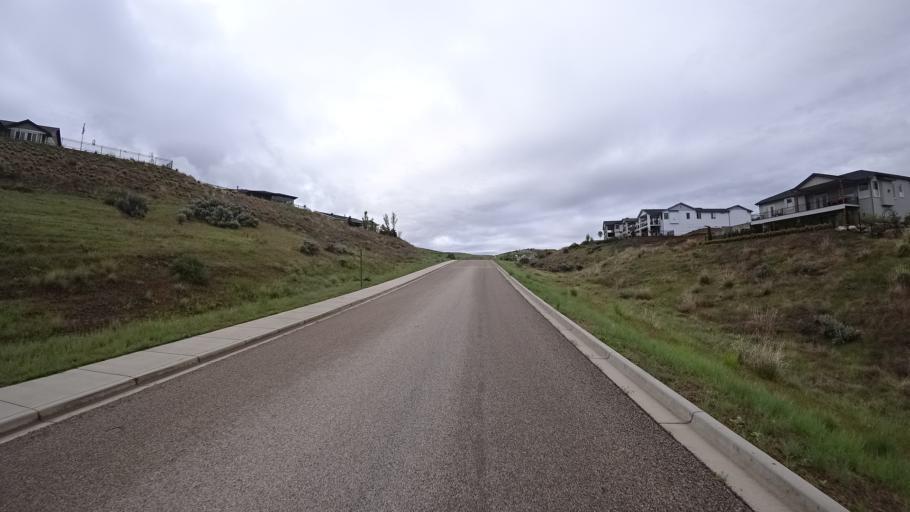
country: US
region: Idaho
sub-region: Ada County
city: Eagle
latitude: 43.7722
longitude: -116.2592
